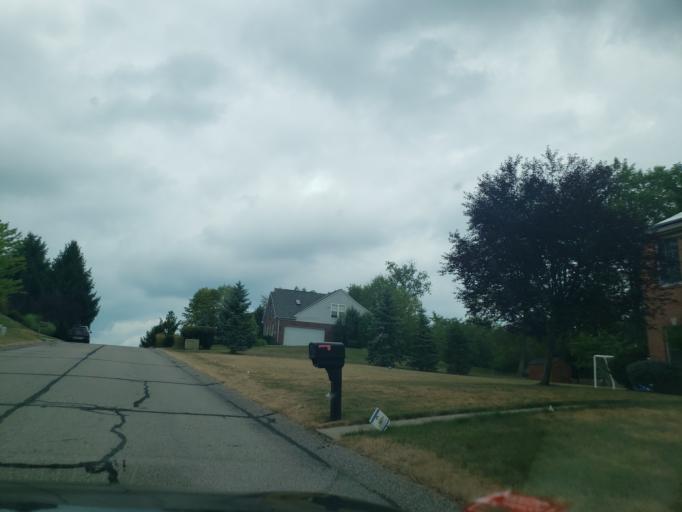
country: US
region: Pennsylvania
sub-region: Allegheny County
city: Coraopolis
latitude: 40.5323
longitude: -80.1622
